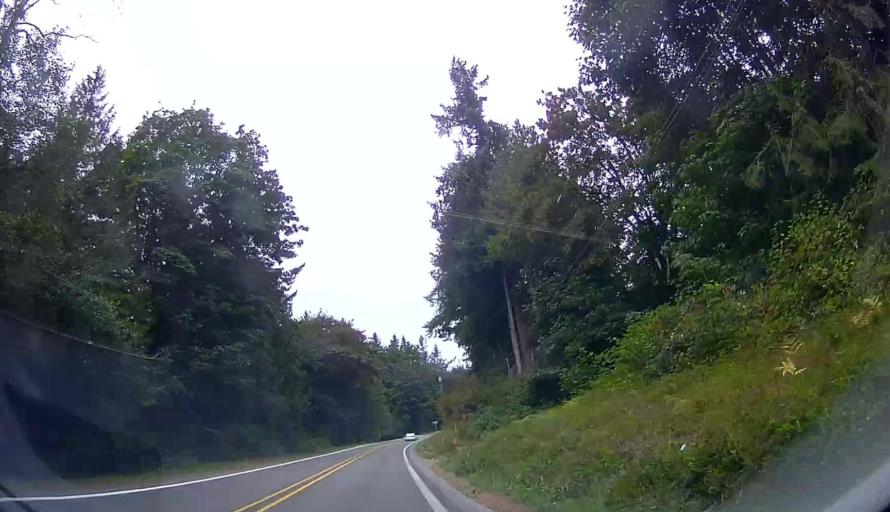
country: US
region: Washington
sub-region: Snohomish County
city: Tulalip
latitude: 48.0992
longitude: -122.3234
